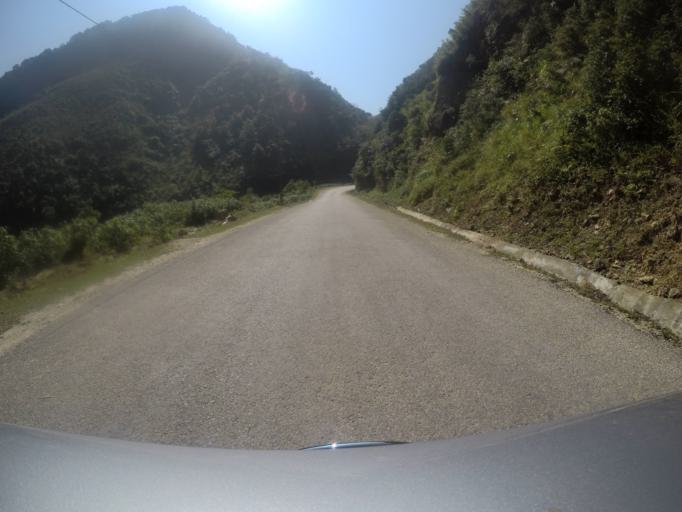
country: VN
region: Lai Chau
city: Than Uyen
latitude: 22.0452
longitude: 103.9577
